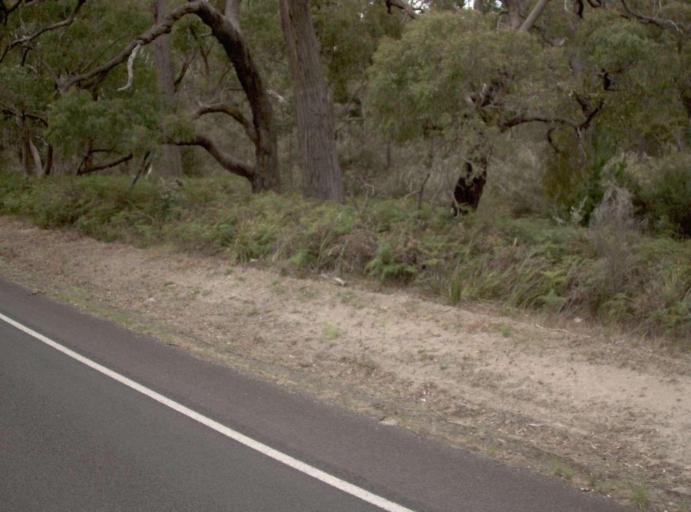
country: AU
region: Victoria
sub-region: Wellington
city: Sale
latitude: -38.2326
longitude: 147.0544
